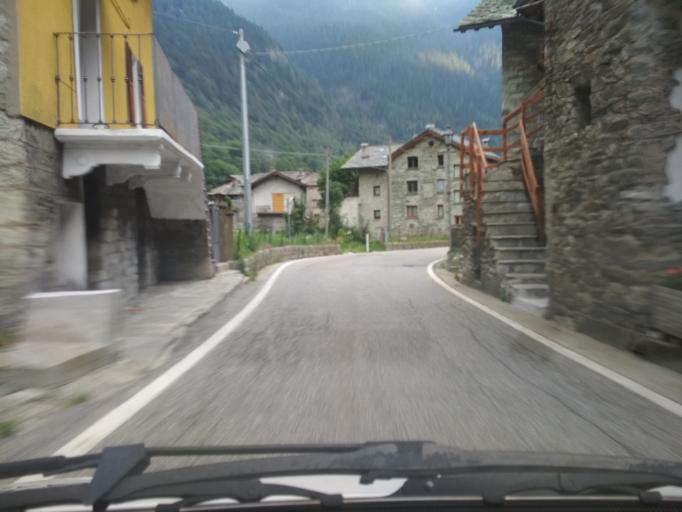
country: IT
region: Aosta Valley
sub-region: Valle d'Aosta
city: Gaby
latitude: 45.7170
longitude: 7.8800
